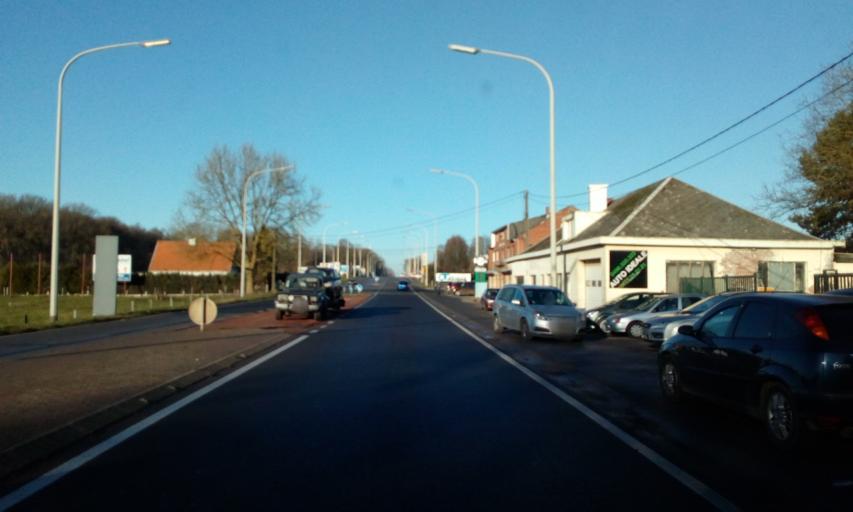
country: BE
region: Wallonia
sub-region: Province du Hainaut
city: Gerpinnes
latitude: 50.3253
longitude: 4.4769
